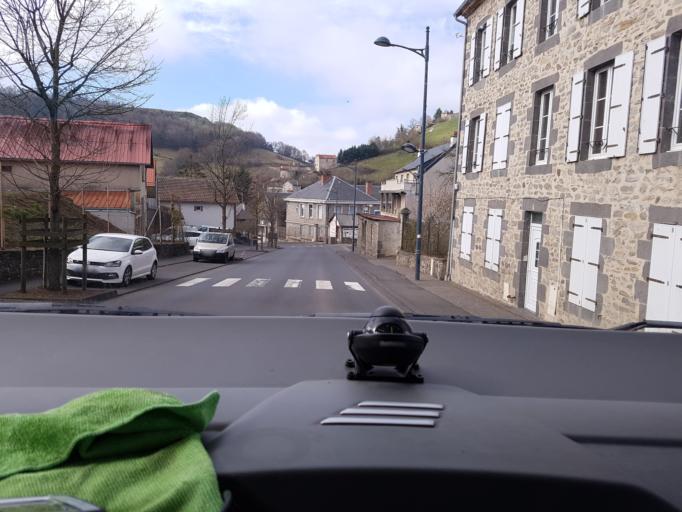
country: FR
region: Auvergne
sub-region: Departement du Cantal
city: Saint-Flour
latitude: 45.0359
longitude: 3.0997
